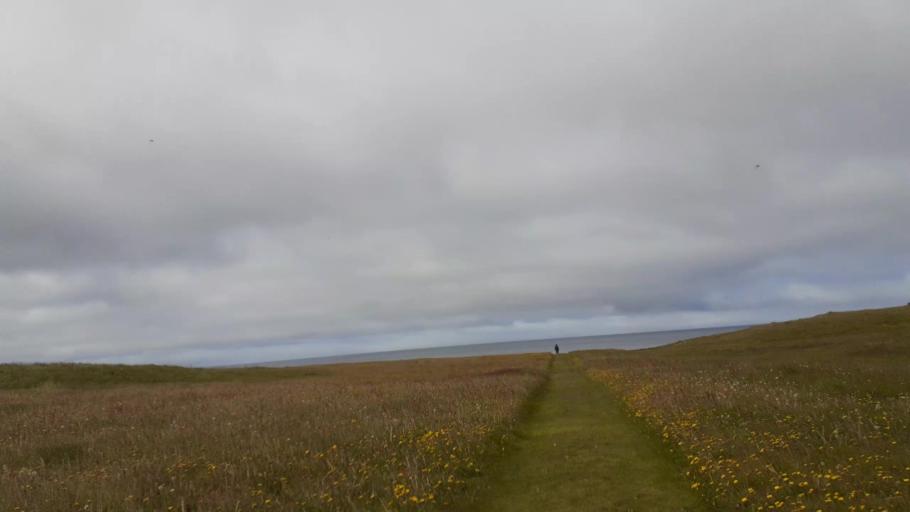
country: IS
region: Northeast
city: Dalvik
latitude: 66.5491
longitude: -18.0233
